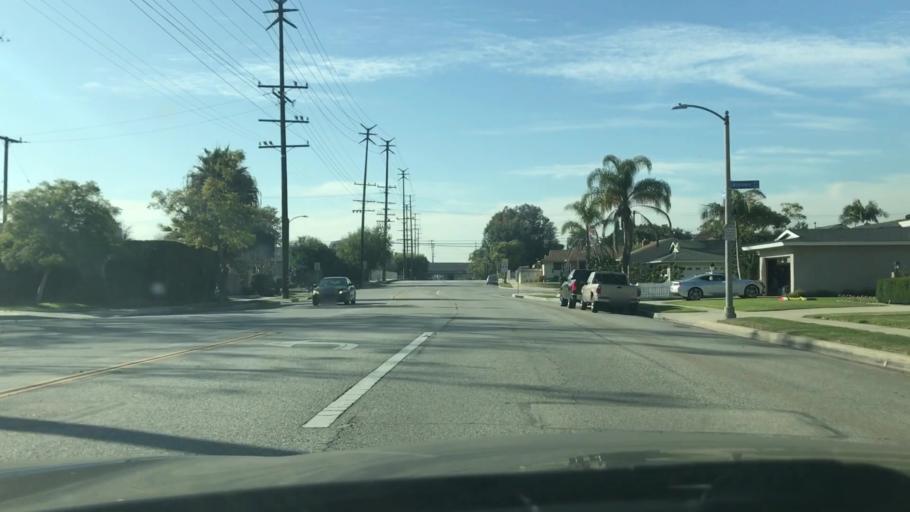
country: US
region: California
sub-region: Orange County
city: Rossmoor
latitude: 33.7956
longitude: -118.1018
